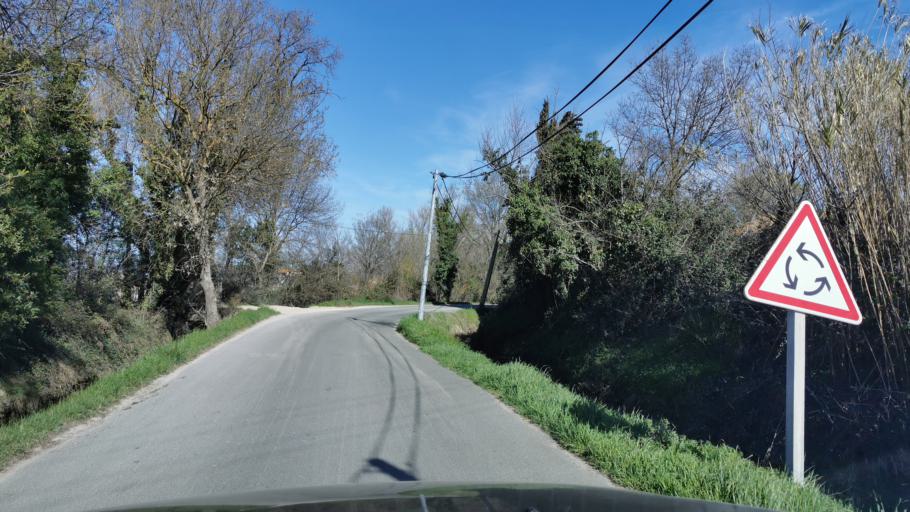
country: FR
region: Languedoc-Roussillon
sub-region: Departement de l'Aude
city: Narbonne
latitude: 43.1928
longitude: 2.9922
